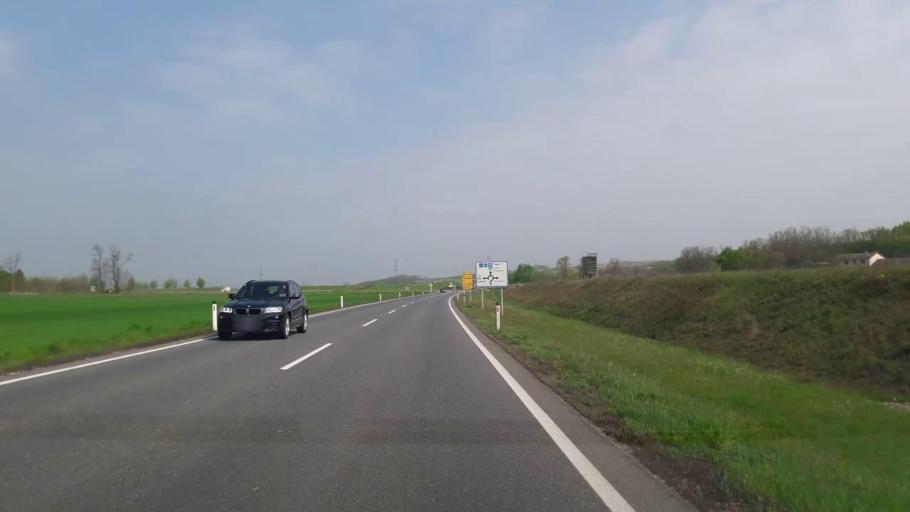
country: AT
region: Lower Austria
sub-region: Politischer Bezirk Hollabrunn
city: Haugsdorf
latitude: 48.7162
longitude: 16.0496
